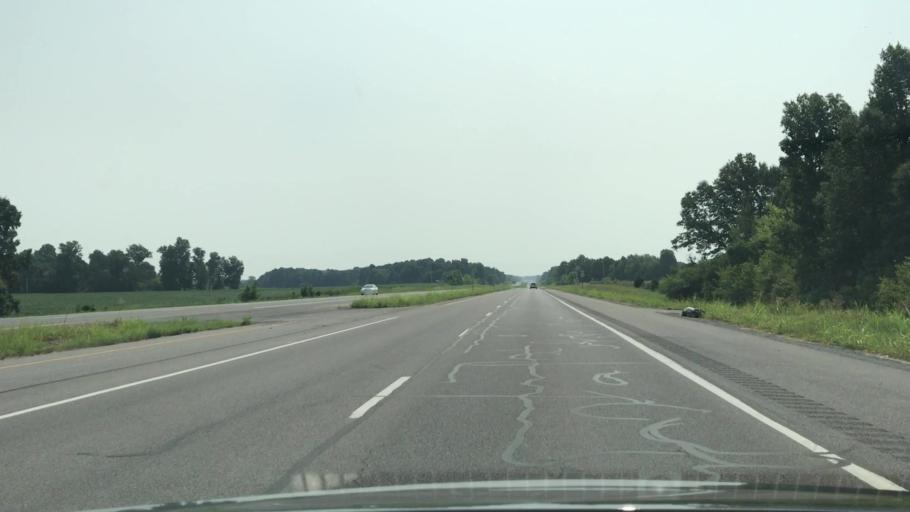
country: US
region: Kentucky
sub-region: Graves County
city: Mayfield
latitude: 36.6761
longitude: -88.5192
